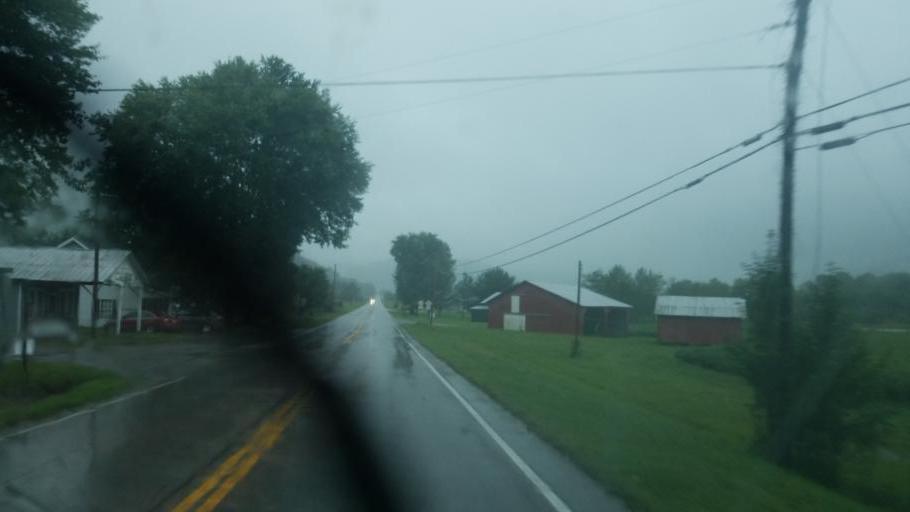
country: US
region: Kentucky
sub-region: Rowan County
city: Morehead
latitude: 38.3014
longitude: -83.5703
